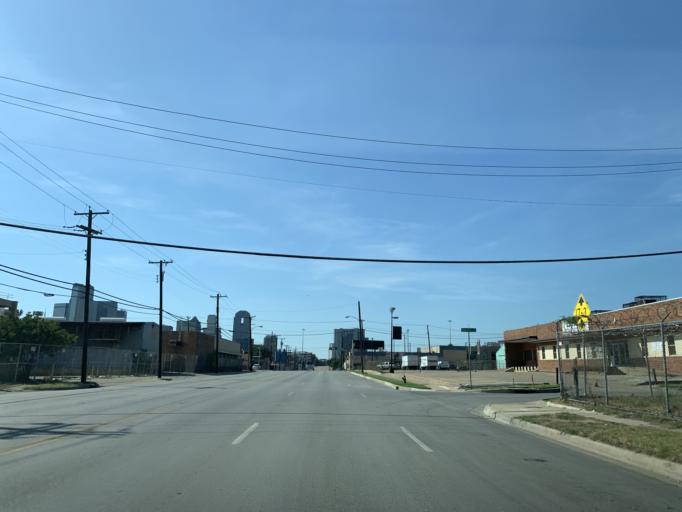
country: US
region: Texas
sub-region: Dallas County
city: Dallas
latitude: 32.7737
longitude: -96.7798
